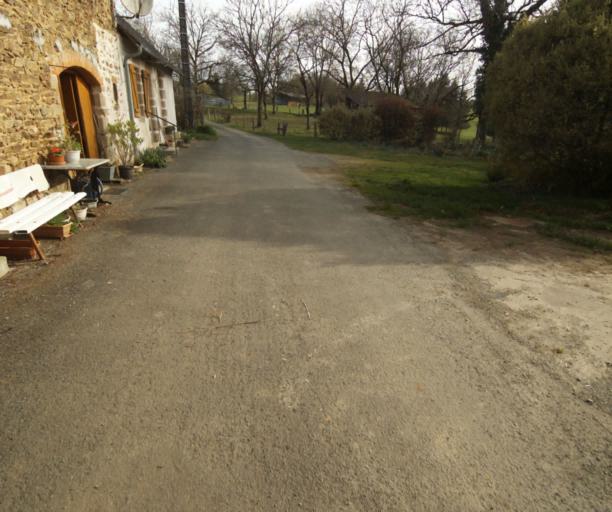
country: FR
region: Limousin
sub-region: Departement de la Correze
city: Chamboulive
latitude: 45.4254
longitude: 1.7601
